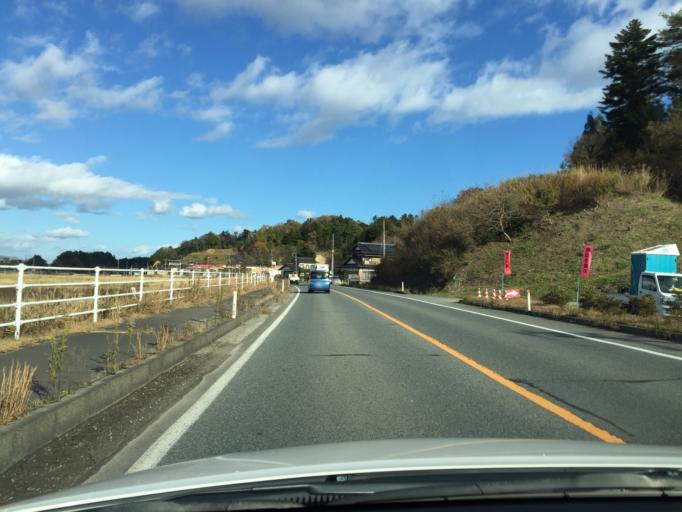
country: JP
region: Fukushima
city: Namie
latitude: 37.5397
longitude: 141.0070
